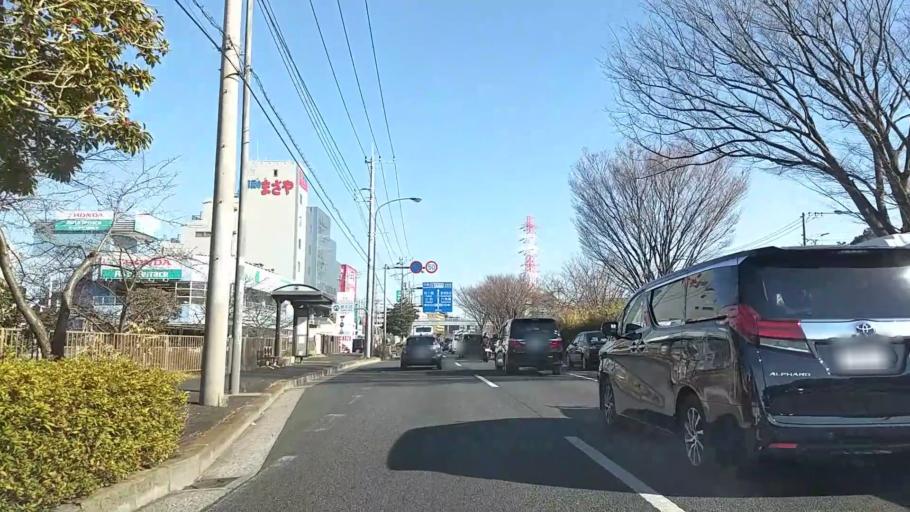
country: JP
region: Kanagawa
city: Yokohama
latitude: 35.4987
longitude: 139.6061
